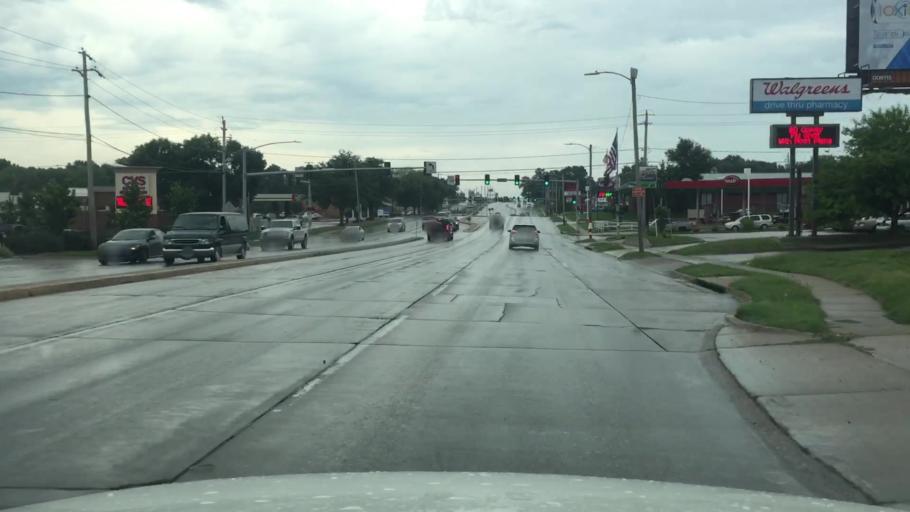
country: US
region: Iowa
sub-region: Polk County
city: Des Moines
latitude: 41.5562
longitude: -93.5970
